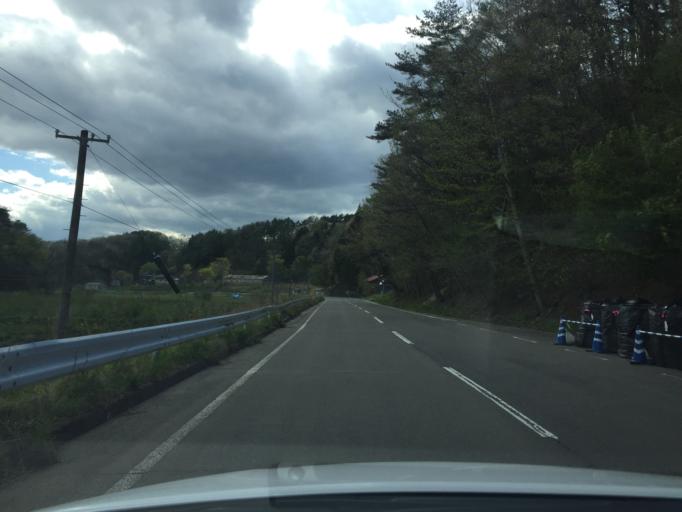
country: JP
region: Miyagi
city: Marumori
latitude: 37.7100
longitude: 140.7675
